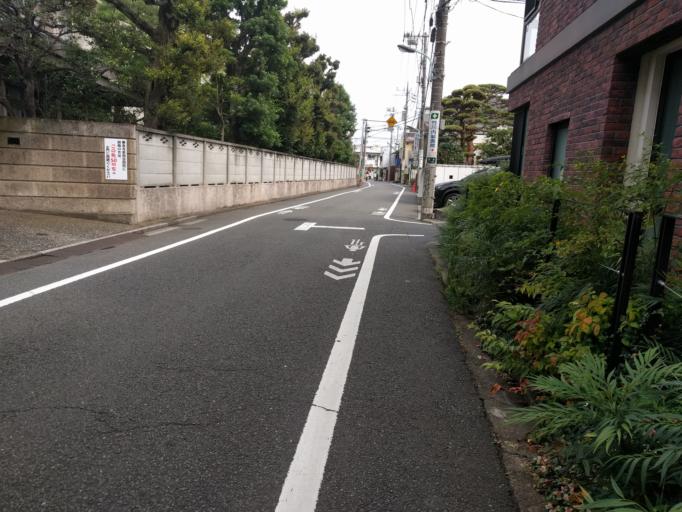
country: JP
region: Tokyo
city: Tokyo
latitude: 35.6508
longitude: 139.6444
